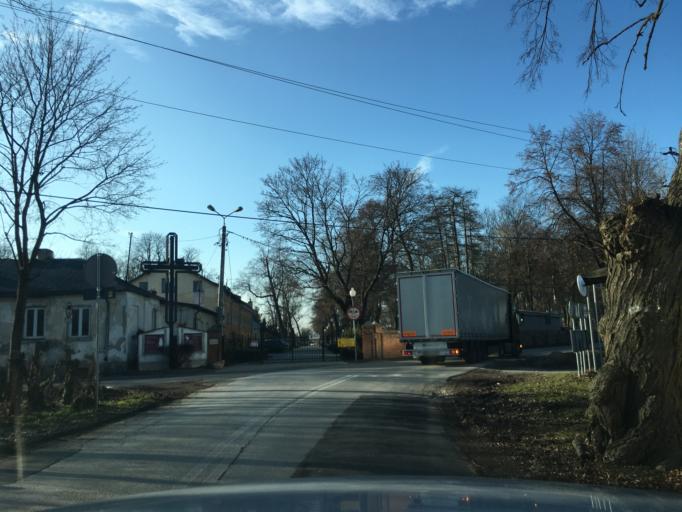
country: PL
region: Masovian Voivodeship
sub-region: Powiat pruszkowski
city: Nadarzyn
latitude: 52.0478
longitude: 20.7859
